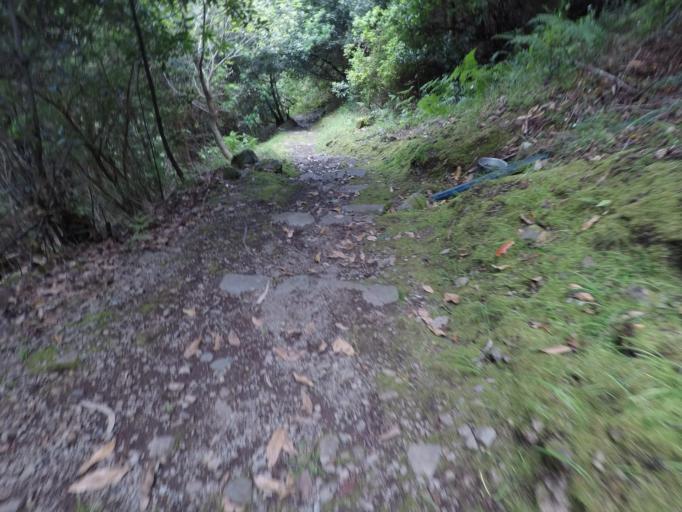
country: PT
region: Madeira
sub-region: Camara de Lobos
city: Curral das Freiras
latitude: 32.7786
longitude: -16.9790
